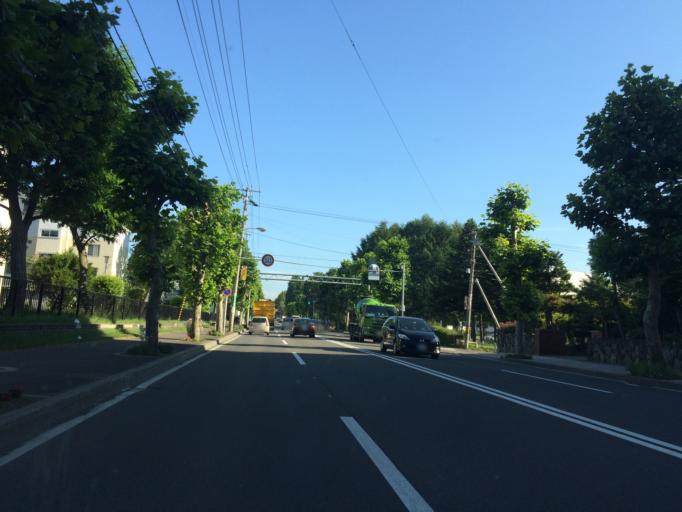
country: JP
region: Hokkaido
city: Sapporo
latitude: 43.0020
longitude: 141.3486
